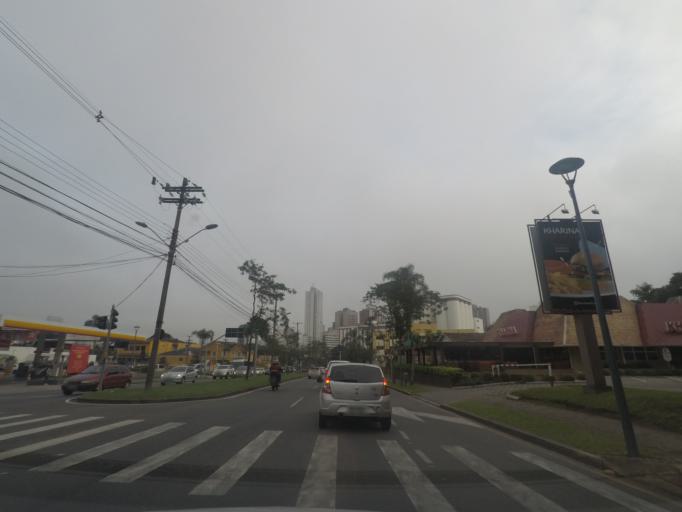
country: BR
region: Parana
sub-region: Curitiba
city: Curitiba
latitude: -25.4385
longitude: -49.2508
